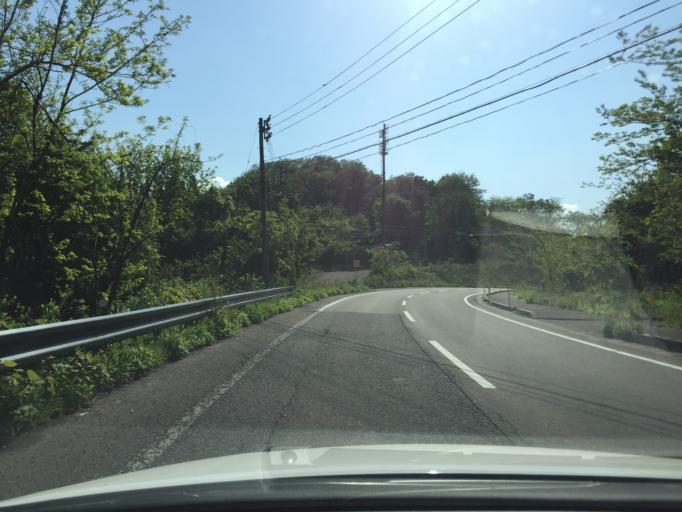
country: JP
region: Niigata
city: Suibara
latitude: 37.7016
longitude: 139.4737
